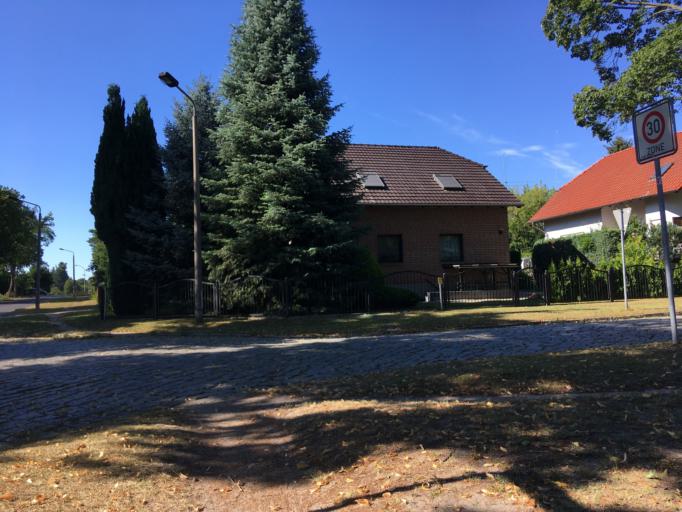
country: DE
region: Brandenburg
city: Zeuthen
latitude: 52.3463
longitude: 13.6022
